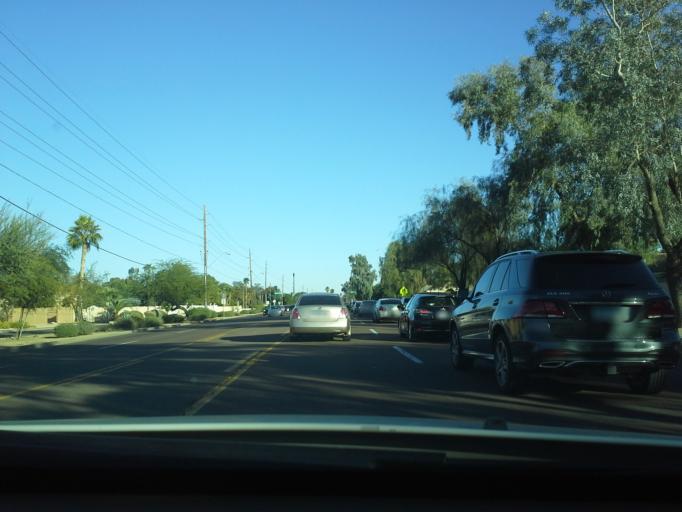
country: US
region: Arizona
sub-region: Maricopa County
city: Paradise Valley
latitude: 33.5826
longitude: -111.9637
